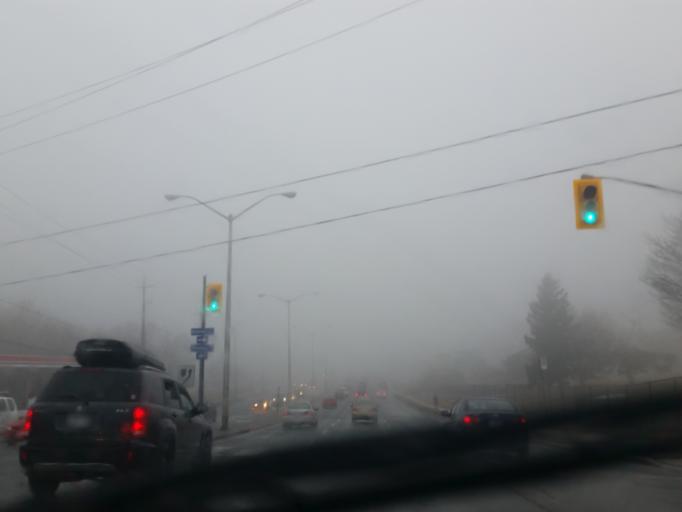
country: CA
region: Ontario
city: Scarborough
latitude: 43.7322
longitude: -79.2247
